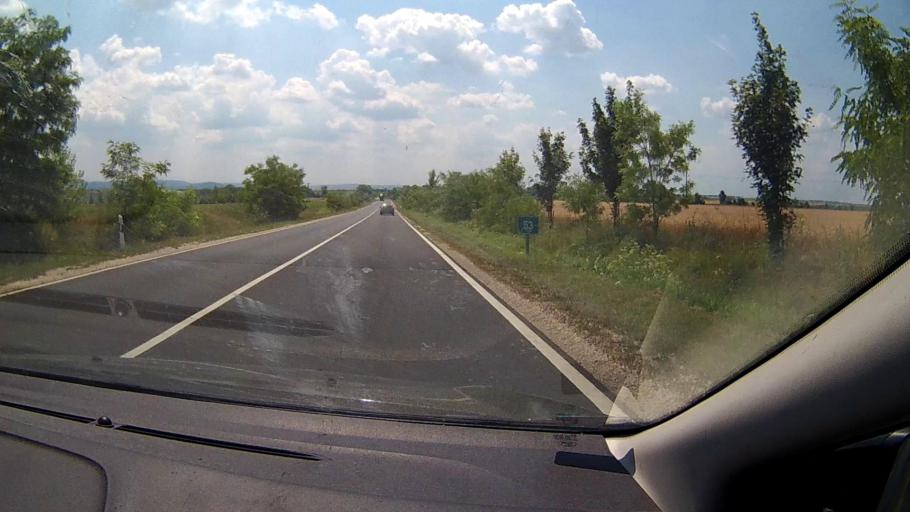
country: HU
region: Komarom-Esztergom
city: Kornye
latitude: 47.5933
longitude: 18.3199
